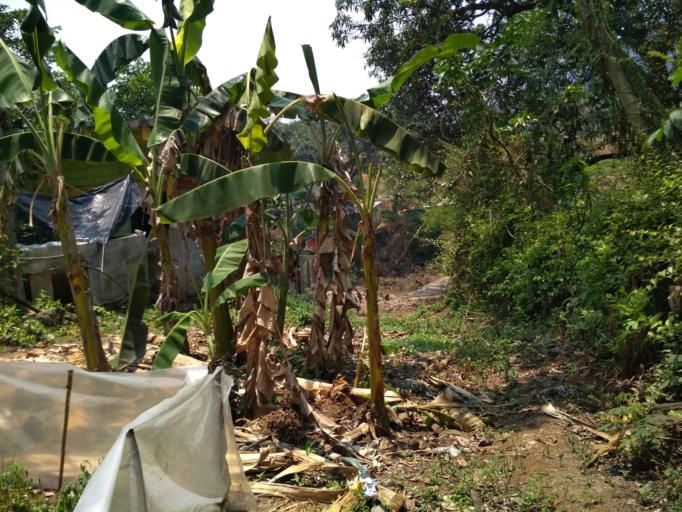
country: MX
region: Veracruz
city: Tezonapa
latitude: 18.6069
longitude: -96.6878
